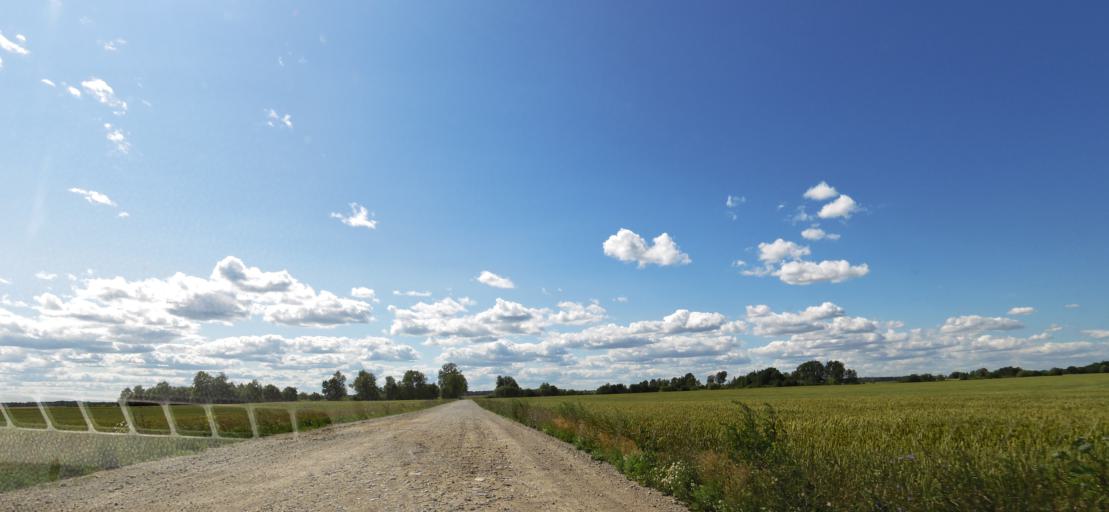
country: LV
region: Bauskas Rajons
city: Bauska
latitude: 56.2407
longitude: 24.2062
